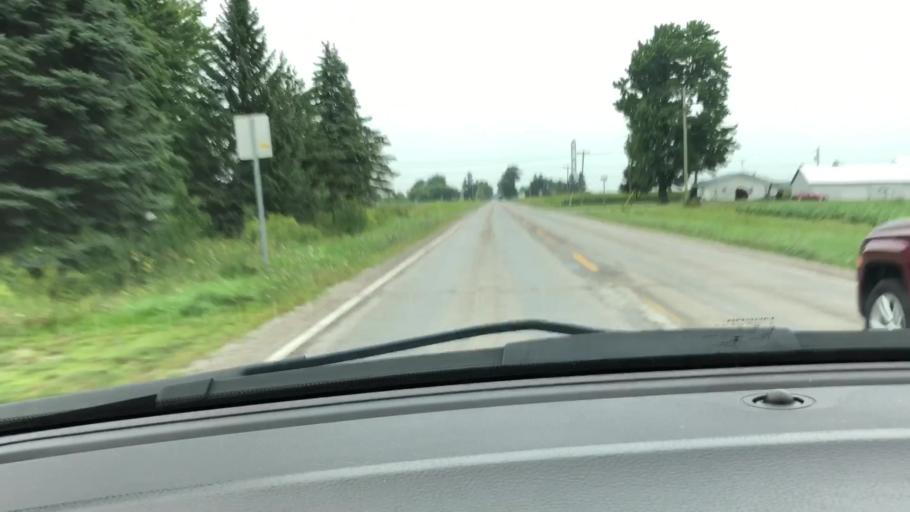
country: US
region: Michigan
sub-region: Saginaw County
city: Freeland
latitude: 43.5528
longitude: -84.0901
